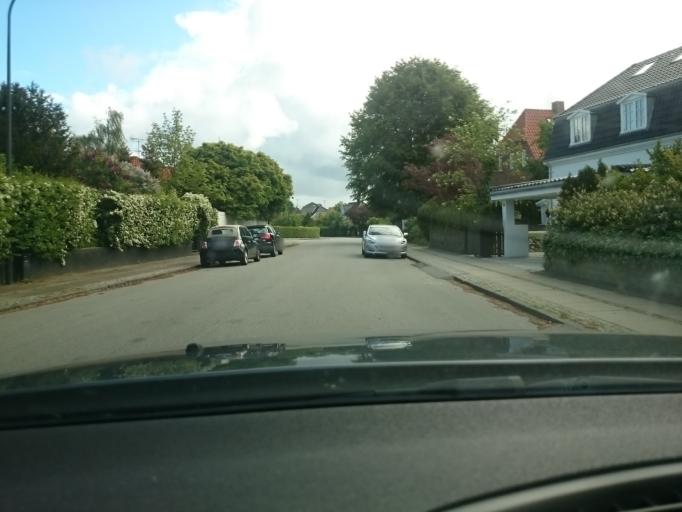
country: DK
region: Capital Region
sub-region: Gentofte Kommune
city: Charlottenlund
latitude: 55.7510
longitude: 12.5595
